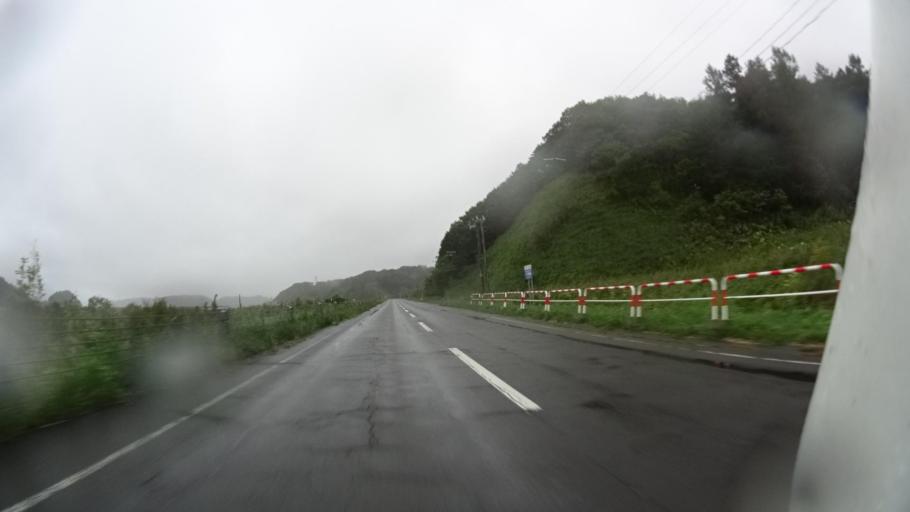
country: JP
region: Hokkaido
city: Kushiro
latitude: 43.0980
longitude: 144.8659
